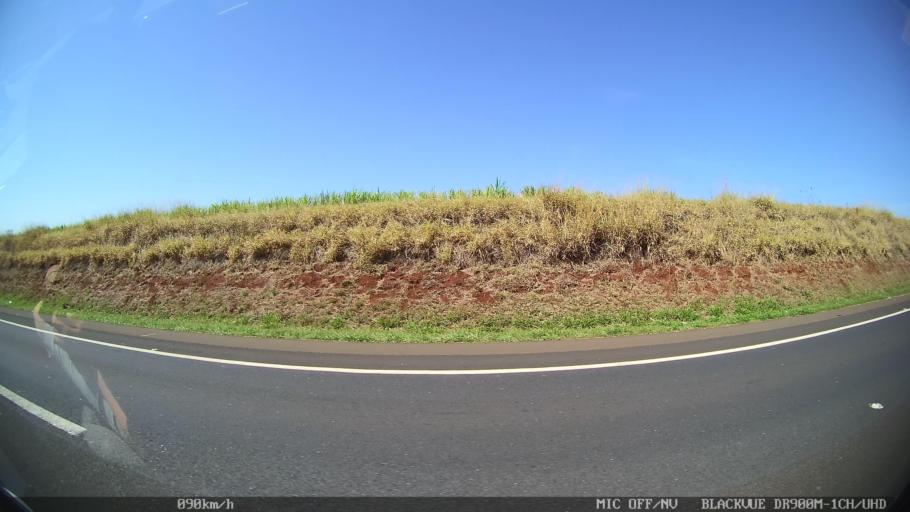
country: BR
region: Sao Paulo
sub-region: Batatais
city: Batatais
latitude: -20.7924
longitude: -47.5615
